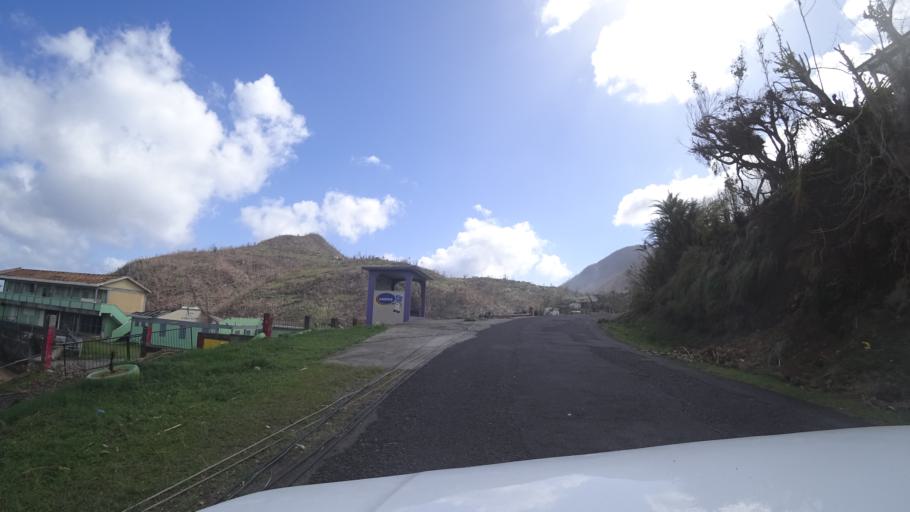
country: DM
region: Saint Patrick
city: Berekua
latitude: 15.2434
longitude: -61.3192
